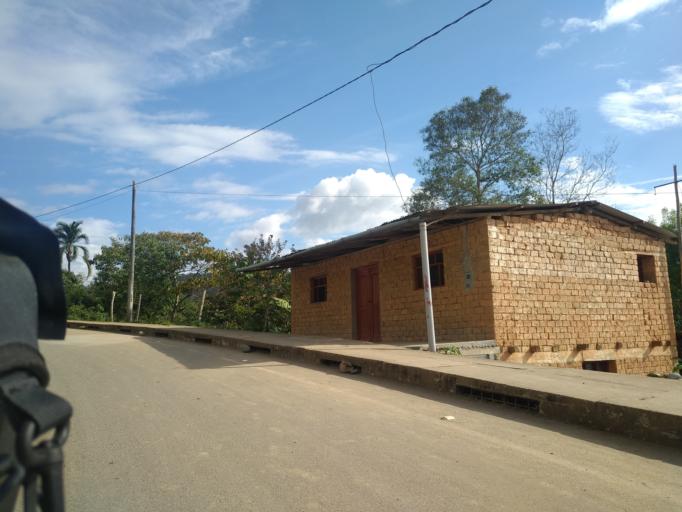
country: PE
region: Cajamarca
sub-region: Provincia de San Ignacio
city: San Ignacio
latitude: -5.1003
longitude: -79.0456
